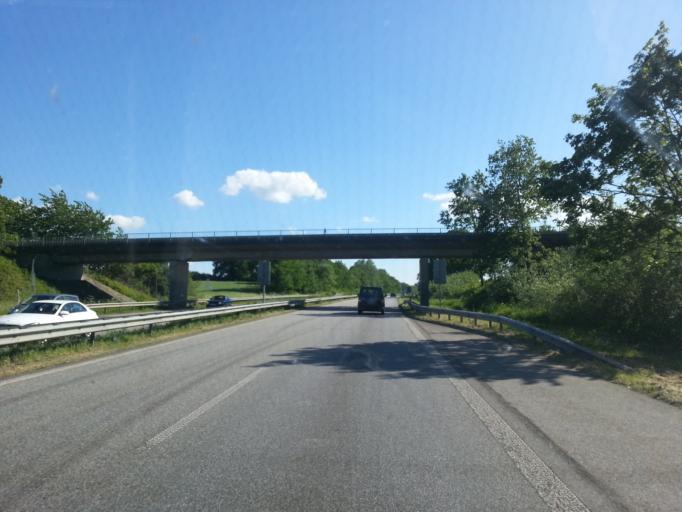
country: DE
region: Schleswig-Holstein
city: Neustadt in Holstein
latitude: 54.1018
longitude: 10.7802
